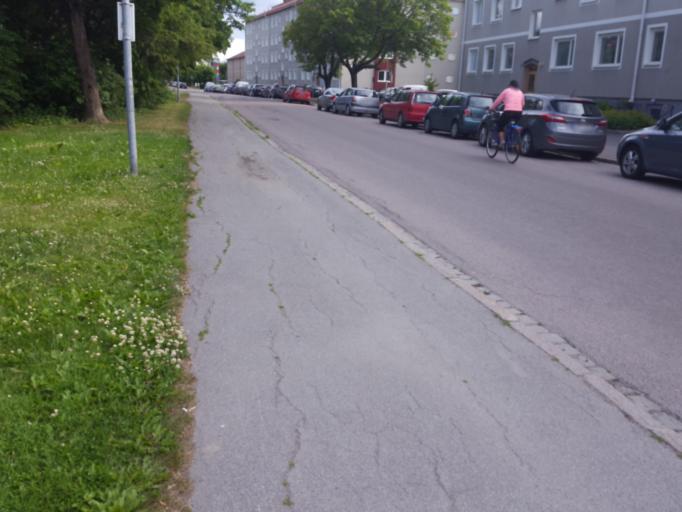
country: SE
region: Uppsala
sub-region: Uppsala Kommun
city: Uppsala
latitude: 59.8657
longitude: 17.6682
